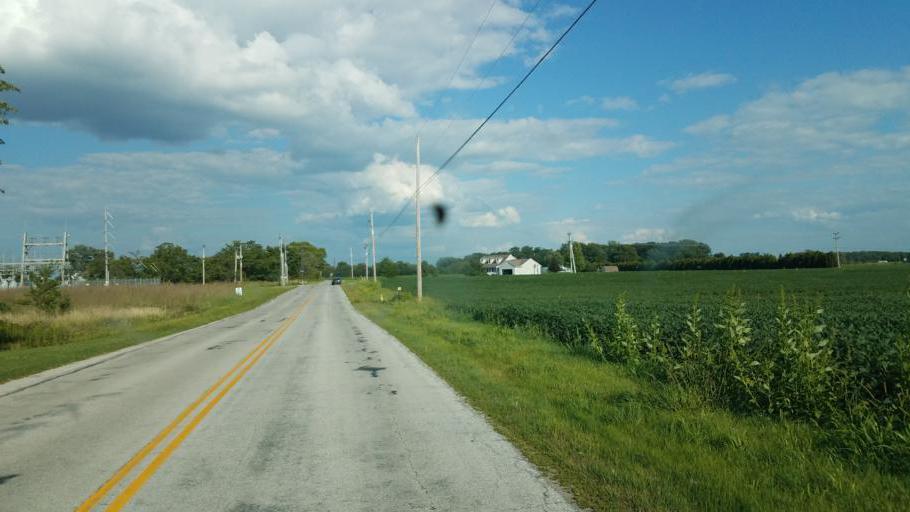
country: US
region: Ohio
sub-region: Wood County
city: Bowling Green
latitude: 41.3610
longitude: -83.5931
